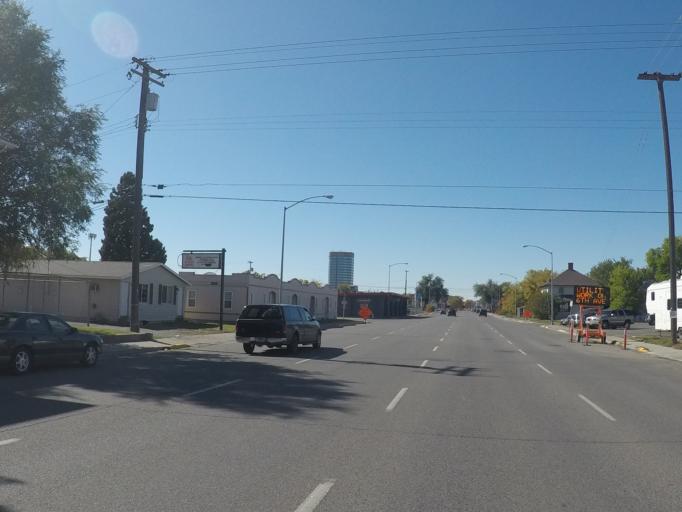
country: US
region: Montana
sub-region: Yellowstone County
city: Billings
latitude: 45.7892
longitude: -108.5042
